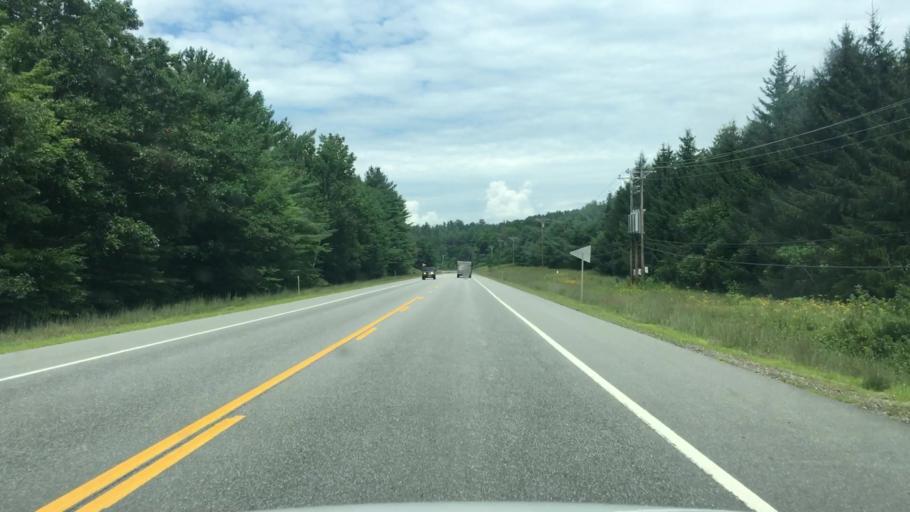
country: US
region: New Hampshire
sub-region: Grafton County
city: Rumney
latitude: 43.8506
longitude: -71.9112
